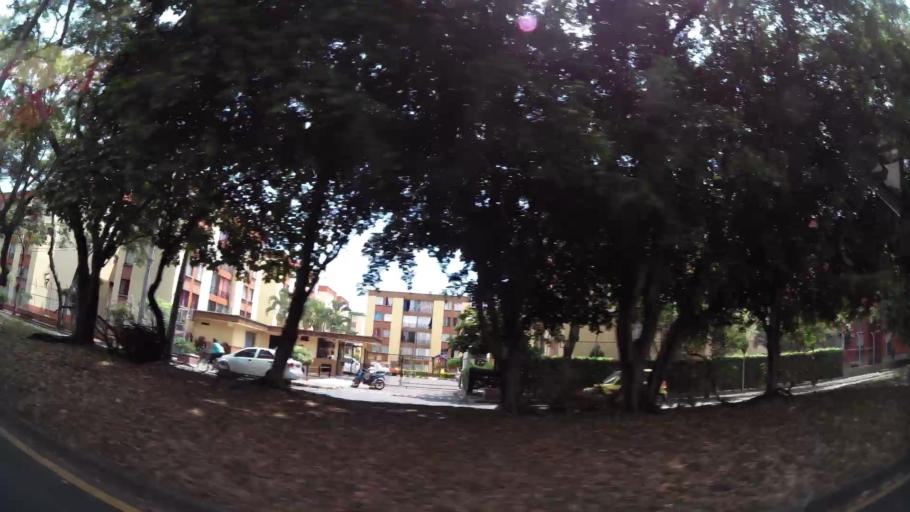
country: CO
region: Valle del Cauca
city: Cali
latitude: 3.4751
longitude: -76.5002
